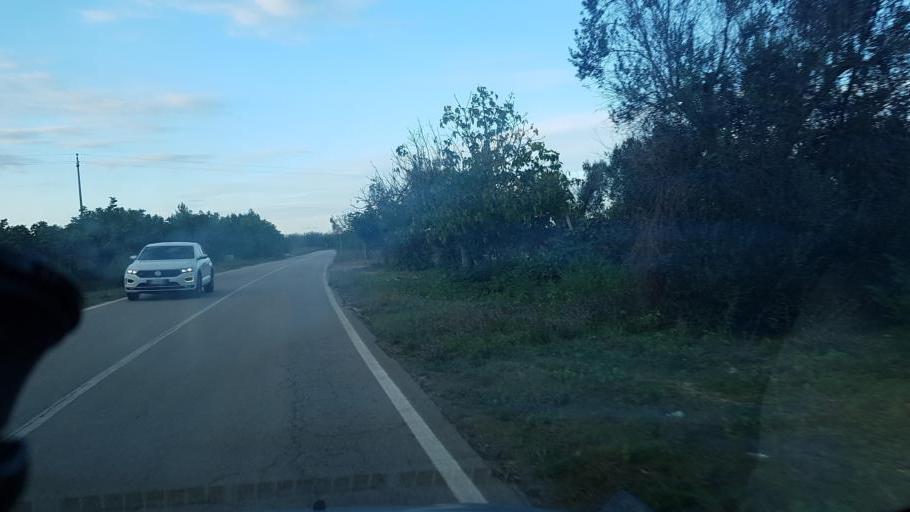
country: IT
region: Apulia
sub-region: Provincia di Lecce
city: Guagnano
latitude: 40.4274
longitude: 17.9499
